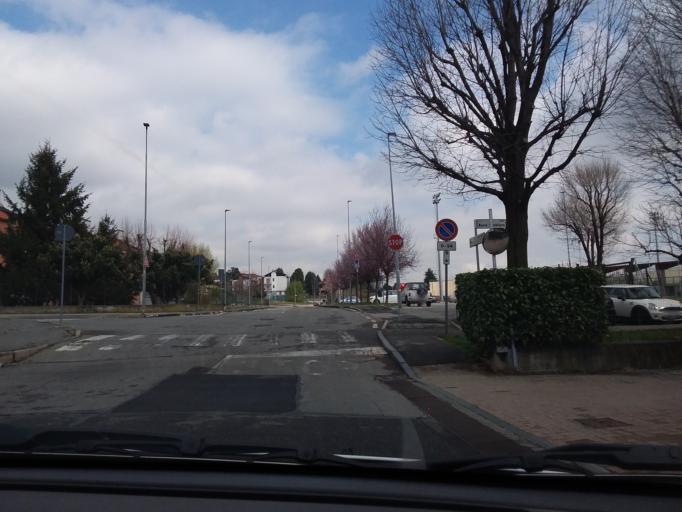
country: IT
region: Piedmont
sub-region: Provincia di Torino
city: Rivoli
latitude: 45.0650
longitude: 7.5276
